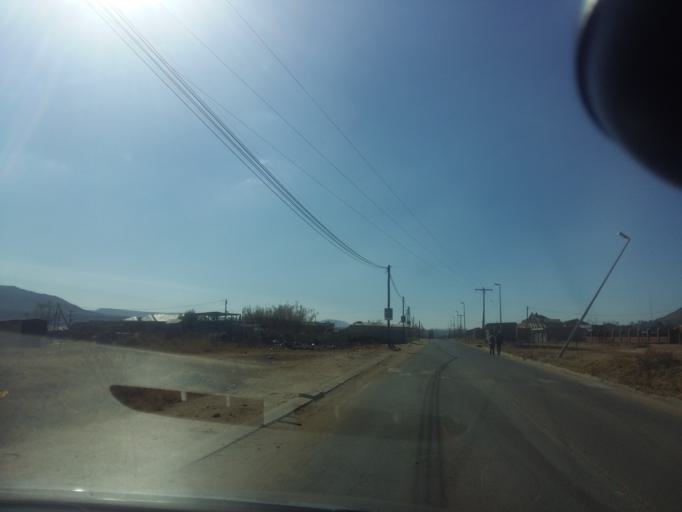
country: LS
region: Maseru
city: Maseru
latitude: -29.3415
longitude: 27.4410
